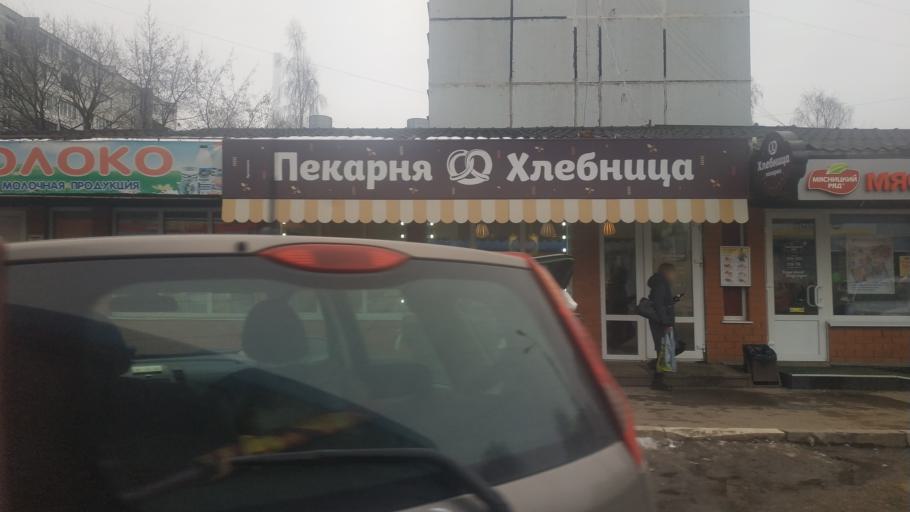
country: RU
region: Tverskaya
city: Tver
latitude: 56.8712
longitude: 35.8885
